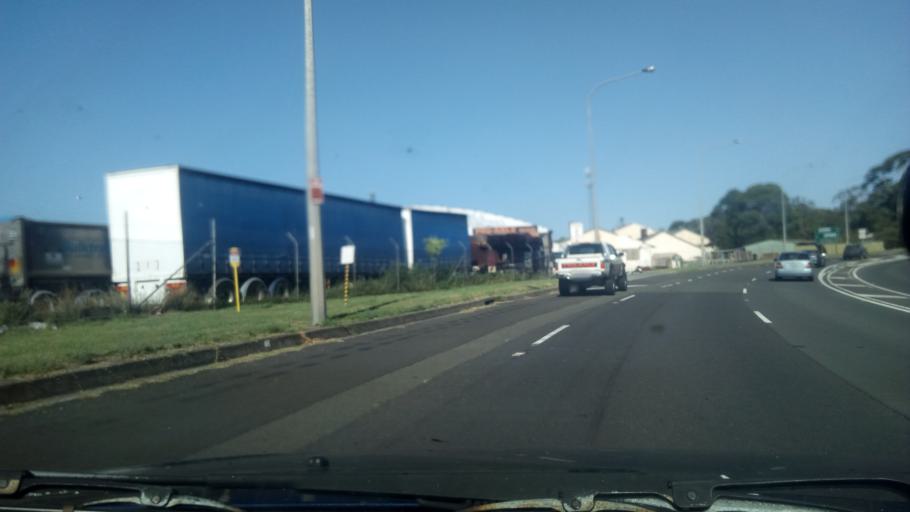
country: AU
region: New South Wales
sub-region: Wollongong
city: Port Kembla
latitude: -34.4781
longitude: 150.8997
